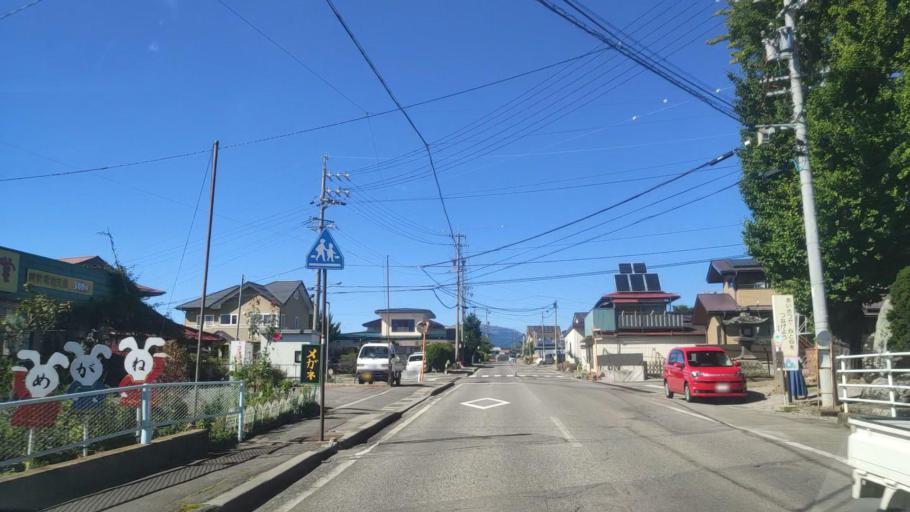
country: JP
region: Nagano
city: Chino
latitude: 35.9743
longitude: 138.2197
